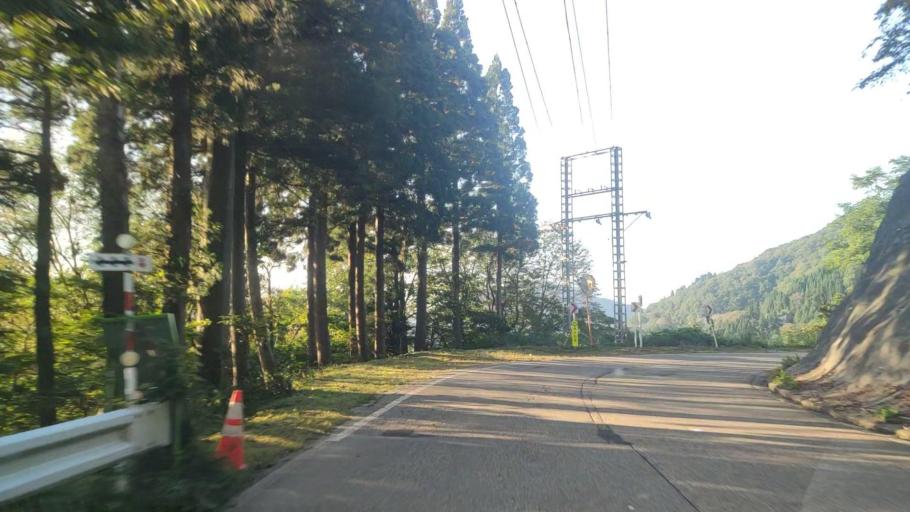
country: JP
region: Toyama
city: Yatsuomachi-higashikumisaka
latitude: 36.4934
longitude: 137.0242
